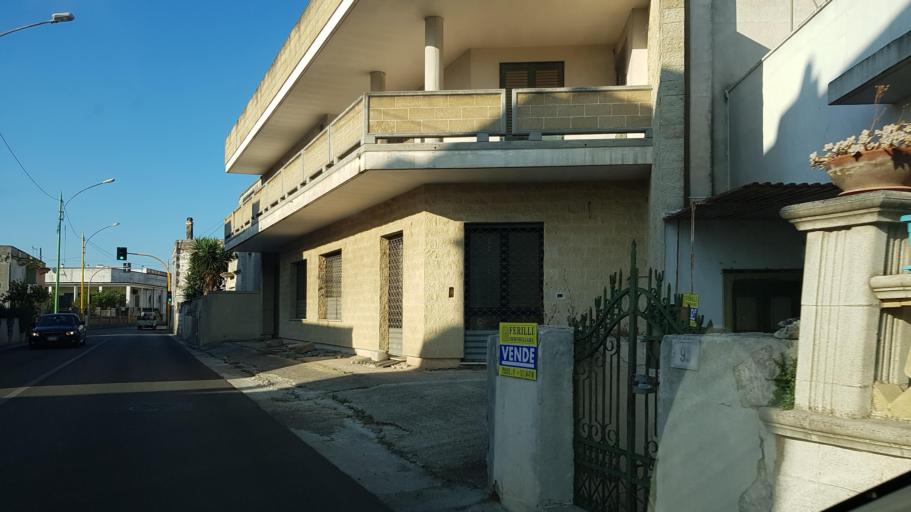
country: IT
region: Apulia
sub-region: Provincia di Lecce
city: Andrano
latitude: 39.9871
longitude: 18.3814
